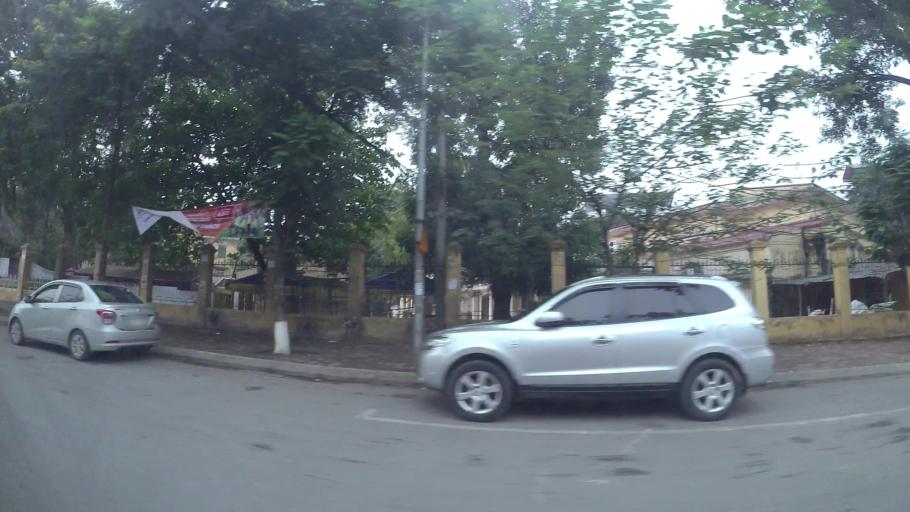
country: VN
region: Ha Noi
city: Hai BaTrung
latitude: 20.9998
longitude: 105.8453
